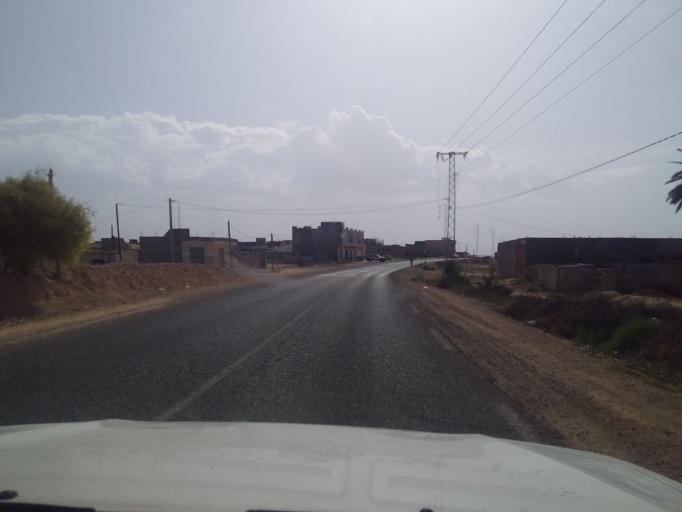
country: TN
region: Qabis
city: Gabes
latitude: 33.6435
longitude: 10.2990
